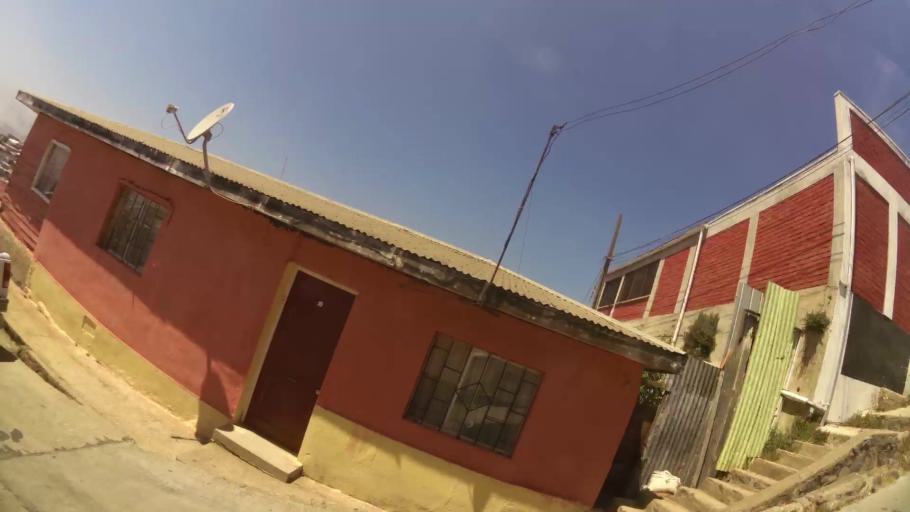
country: CL
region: Valparaiso
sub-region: Provincia de Valparaiso
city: Valparaiso
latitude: -33.0409
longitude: -71.6416
